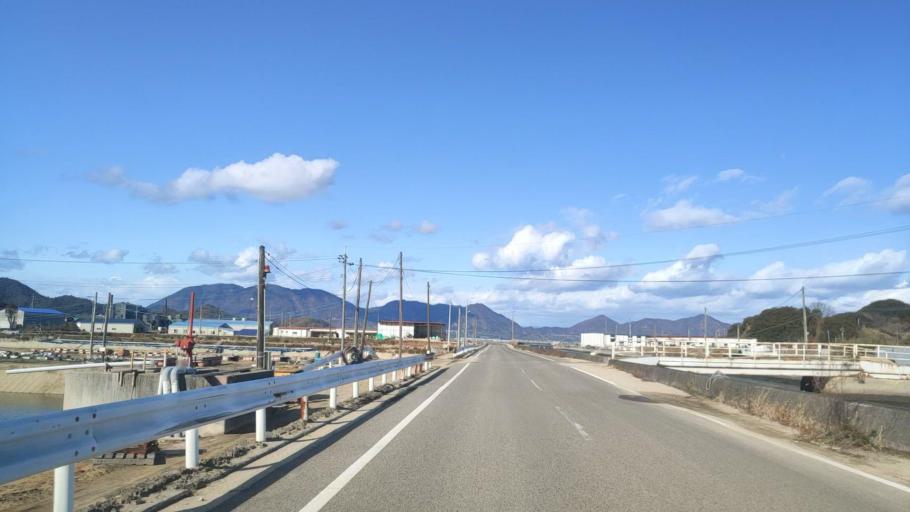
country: JP
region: Hiroshima
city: Innoshima
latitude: 34.2135
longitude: 133.1220
